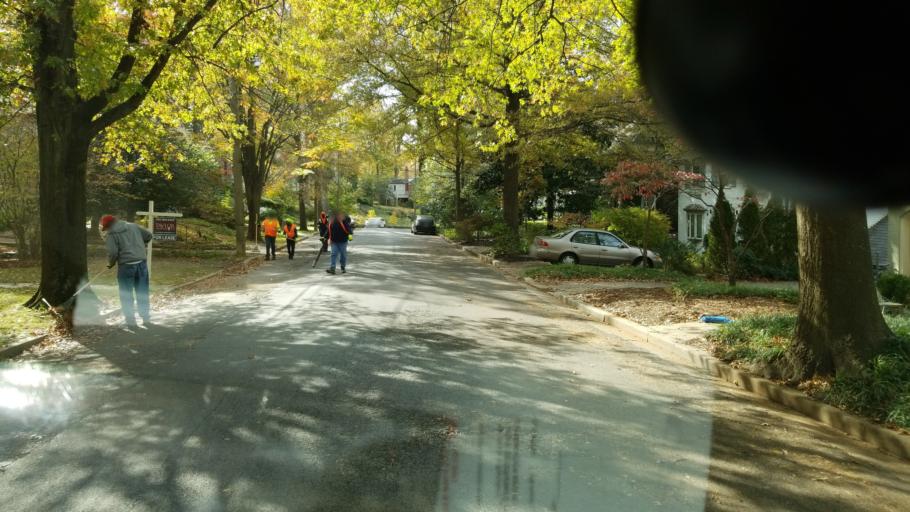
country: US
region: Maryland
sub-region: Montgomery County
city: Chevy Chase
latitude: 38.9755
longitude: -77.0597
